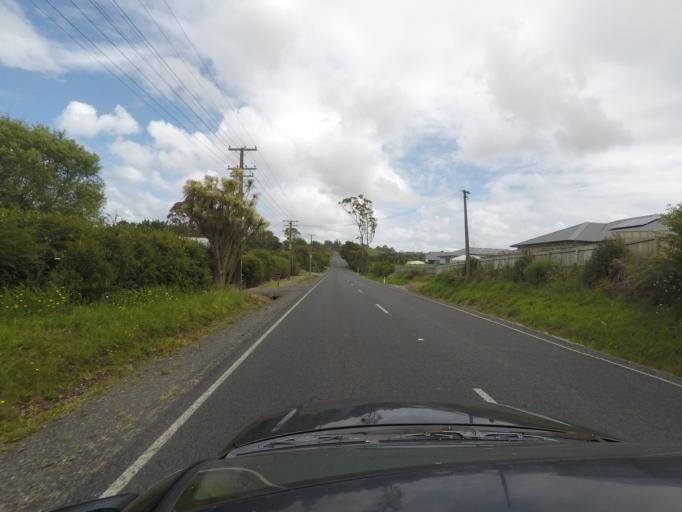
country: NZ
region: Auckland
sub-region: Auckland
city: Parakai
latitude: -36.6290
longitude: 174.5026
